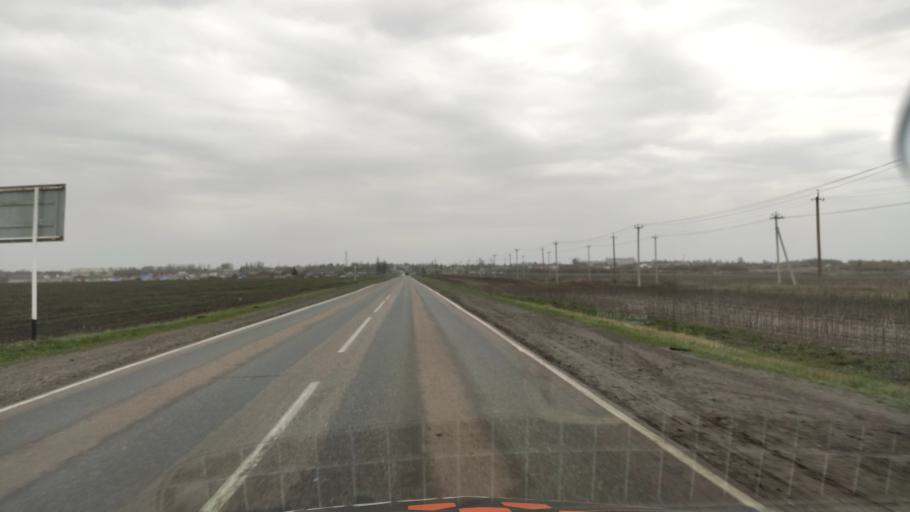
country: RU
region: Kursk
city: Gorshechnoye
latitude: 51.5091
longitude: 37.9987
